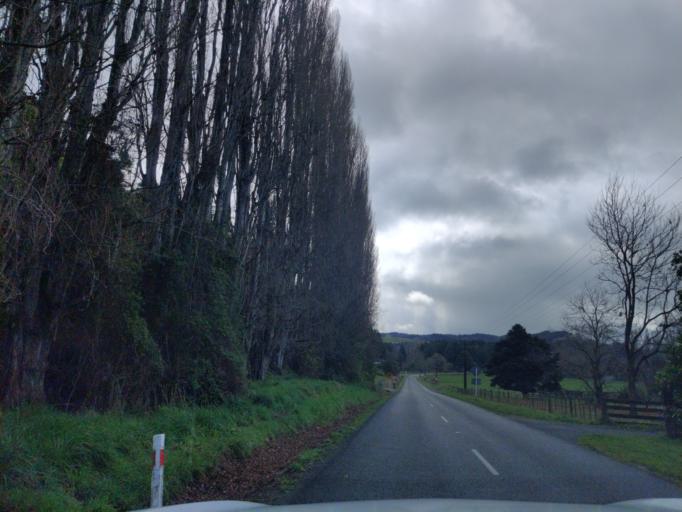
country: NZ
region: Manawatu-Wanganui
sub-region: Palmerston North City
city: Palmerston North
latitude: -40.1801
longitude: 175.7887
